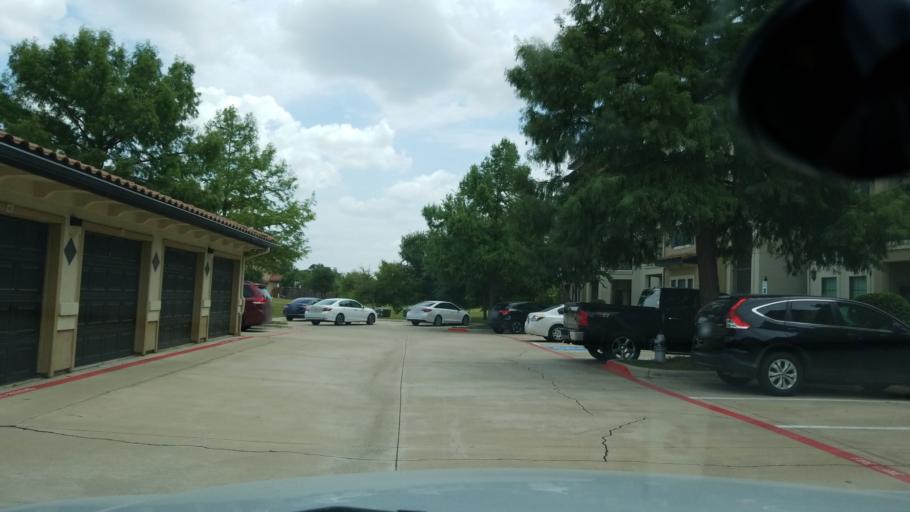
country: US
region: Texas
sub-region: Dallas County
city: Farmers Branch
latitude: 32.8963
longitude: -96.9325
